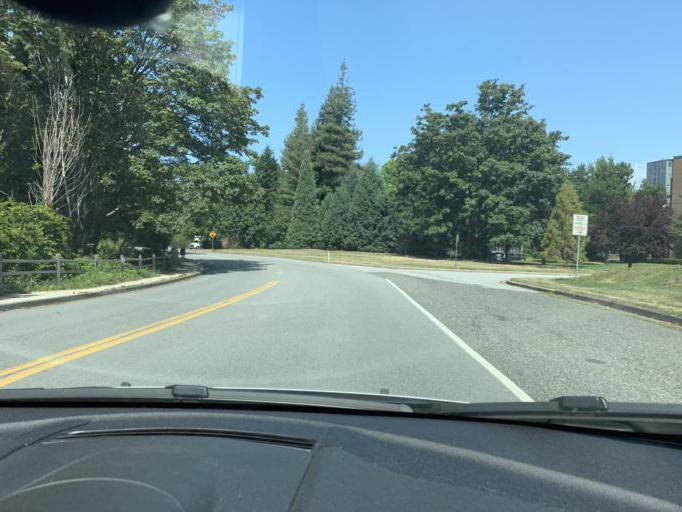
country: CA
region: British Columbia
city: West End
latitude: 49.2611
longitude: -123.2576
